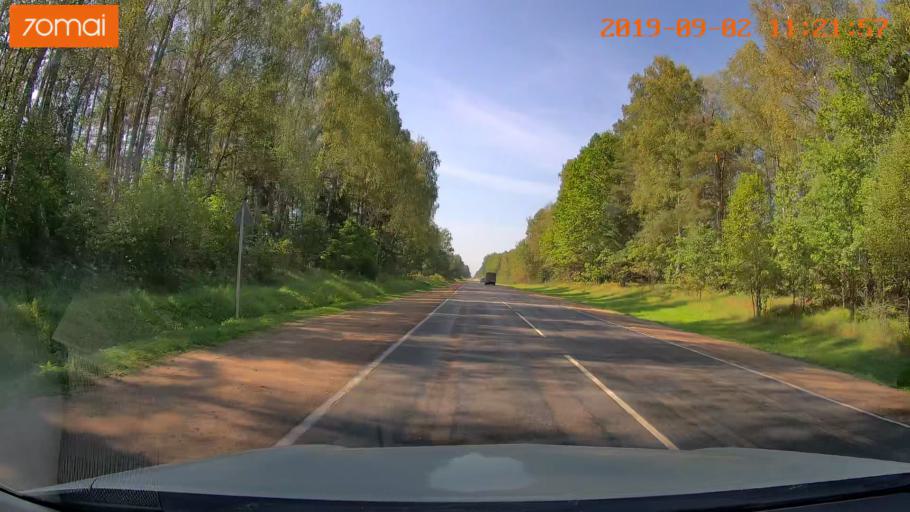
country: RU
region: Smolensk
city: Roslavl'
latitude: 54.0302
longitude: 33.0243
